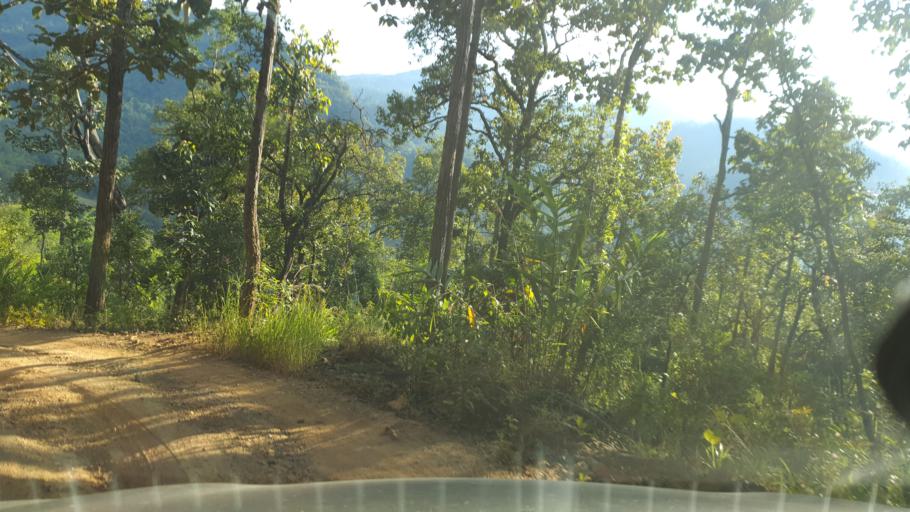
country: TH
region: Chiang Mai
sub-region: Amphoe Chiang Dao
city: Chiang Dao
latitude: 19.4103
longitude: 98.8317
